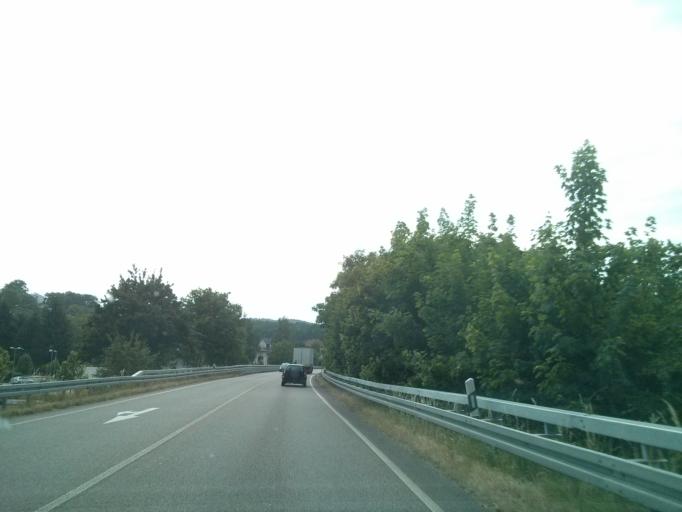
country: DE
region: Baden-Wuerttemberg
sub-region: Karlsruhe Region
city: Gaggenau
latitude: 48.7998
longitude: 8.3179
